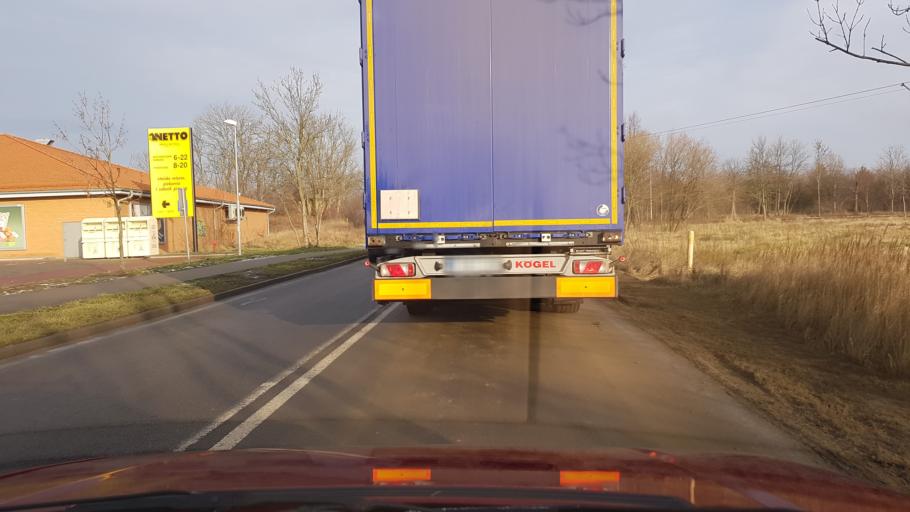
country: PL
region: West Pomeranian Voivodeship
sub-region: Powiat policki
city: Police
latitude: 53.4951
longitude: 14.5835
